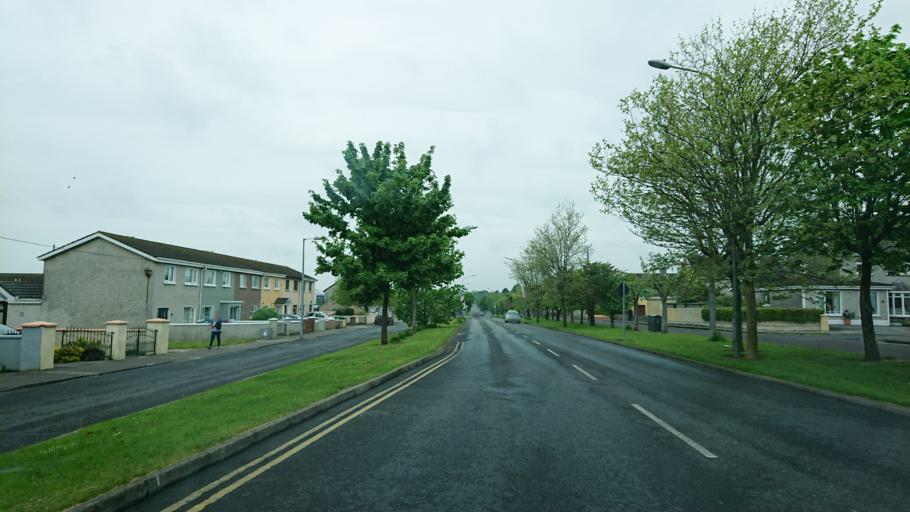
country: IE
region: Munster
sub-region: Waterford
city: Waterford
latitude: 52.2495
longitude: -7.1391
